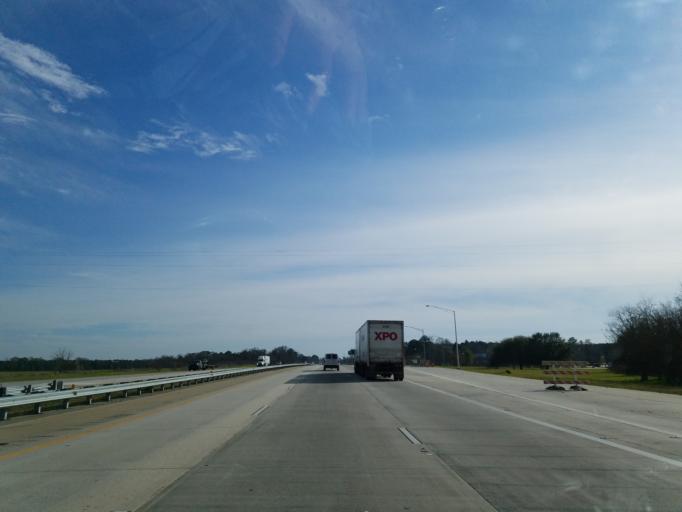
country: US
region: Georgia
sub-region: Dooly County
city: Unadilla
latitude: 32.2128
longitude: -83.7457
